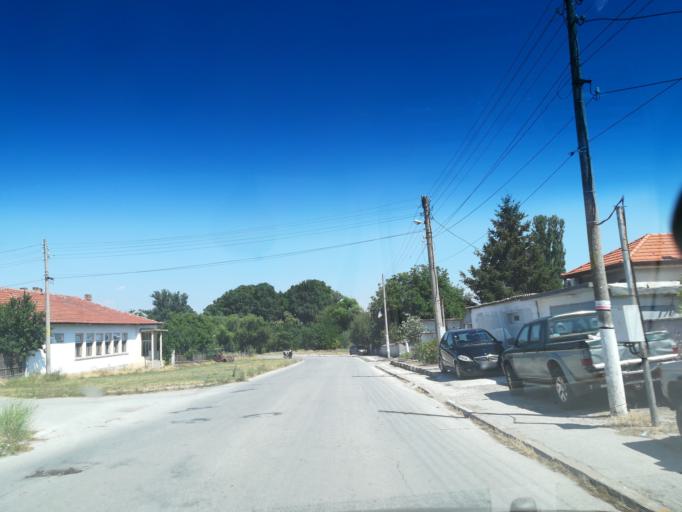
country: BG
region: Plovdiv
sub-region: Obshtina Sadovo
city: Sadovo
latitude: 42.0227
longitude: 25.1002
